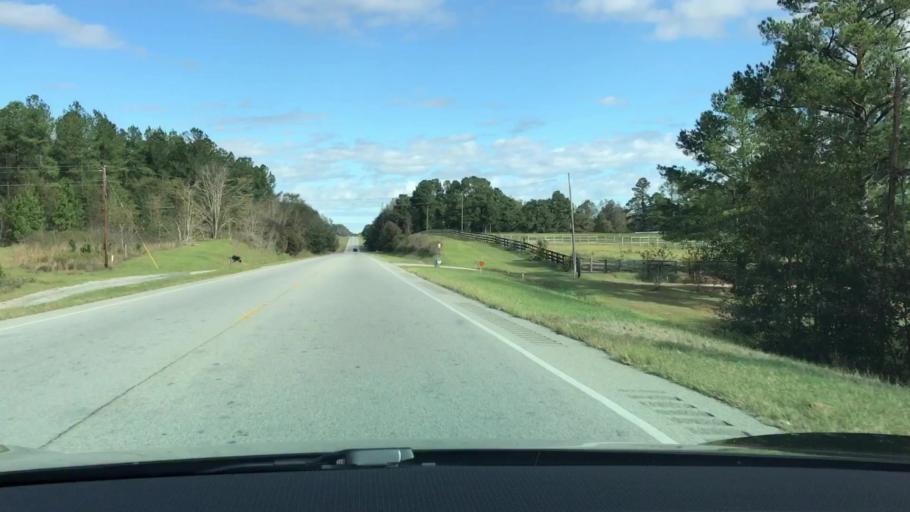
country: US
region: Georgia
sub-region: Jefferson County
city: Louisville
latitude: 32.9376
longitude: -82.3960
